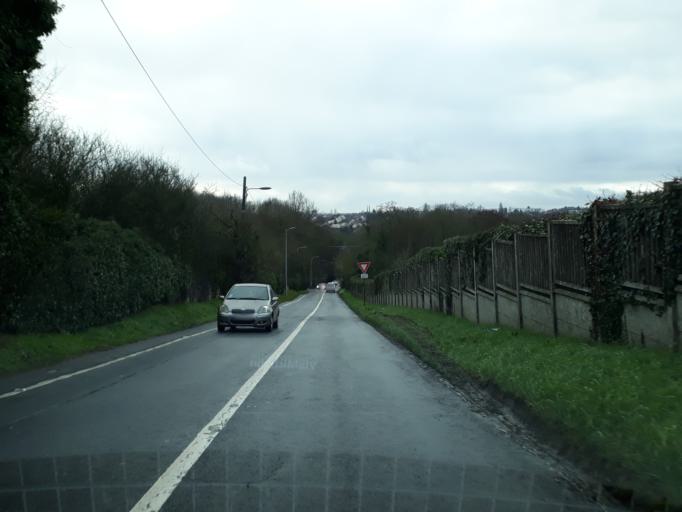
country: FR
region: Ile-de-France
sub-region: Departement de l'Essonne
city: Villabe
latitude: 48.5827
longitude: 2.4428
